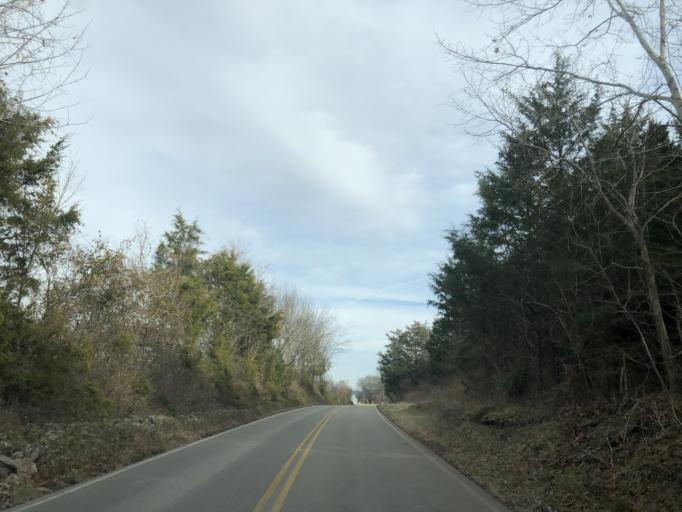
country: US
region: Tennessee
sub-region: Williamson County
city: Franklin
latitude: 35.9364
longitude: -86.9082
